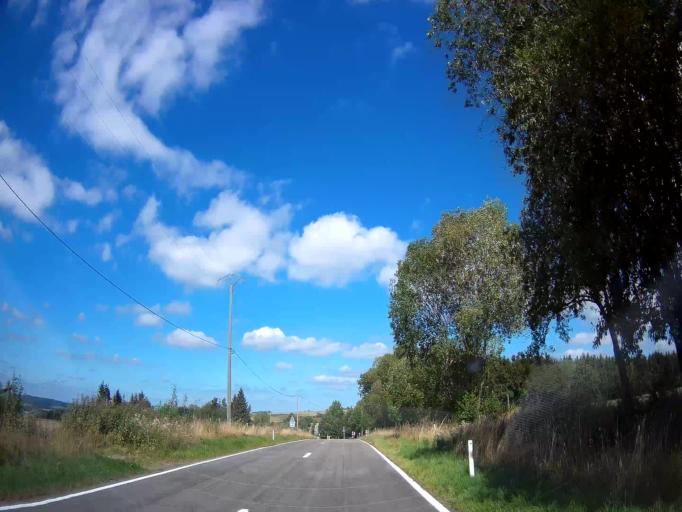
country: BE
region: Wallonia
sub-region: Province du Luxembourg
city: Bertogne
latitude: 50.0441
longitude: 5.6889
